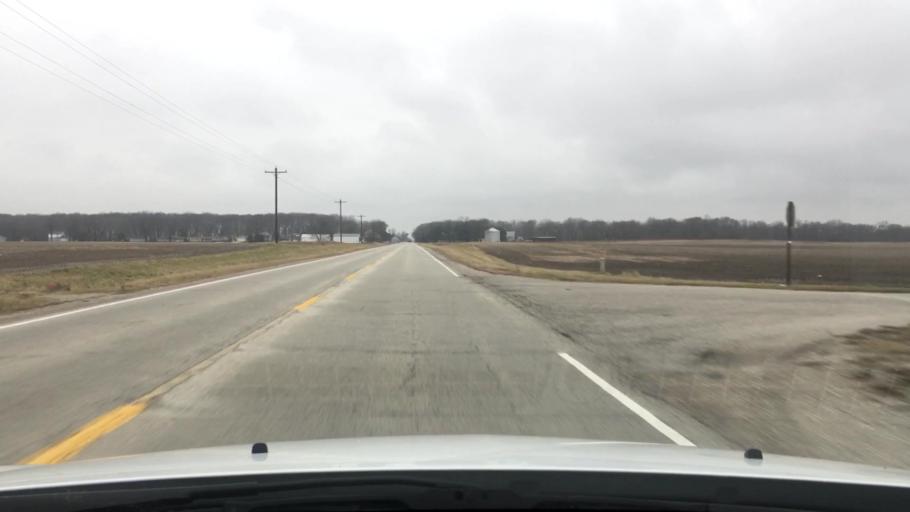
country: US
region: Illinois
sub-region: Iroquois County
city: Clifton
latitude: 40.8880
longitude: -87.8224
